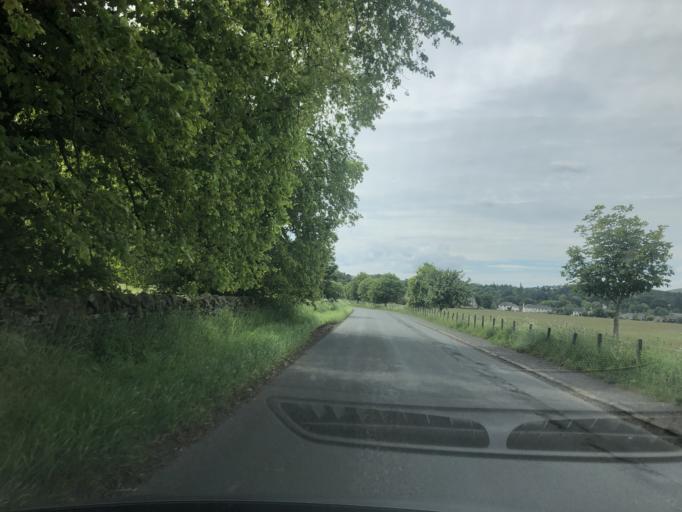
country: GB
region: Scotland
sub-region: The Scottish Borders
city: West Linton
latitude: 55.7456
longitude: -3.3489
